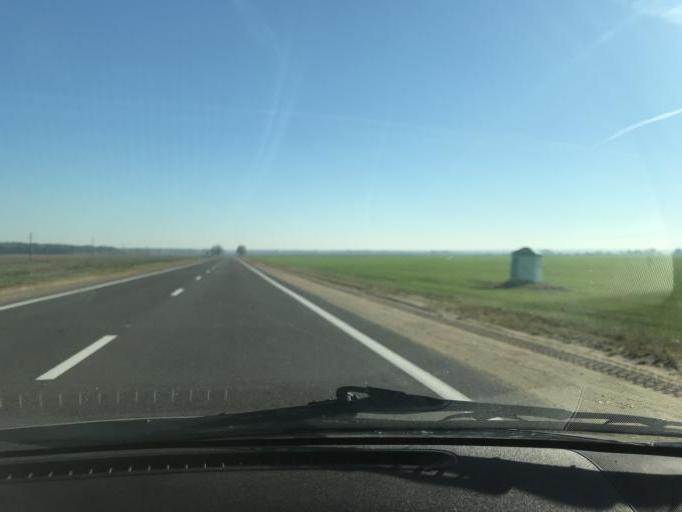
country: BY
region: Brest
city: Ivanava
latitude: 52.1561
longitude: 25.6534
